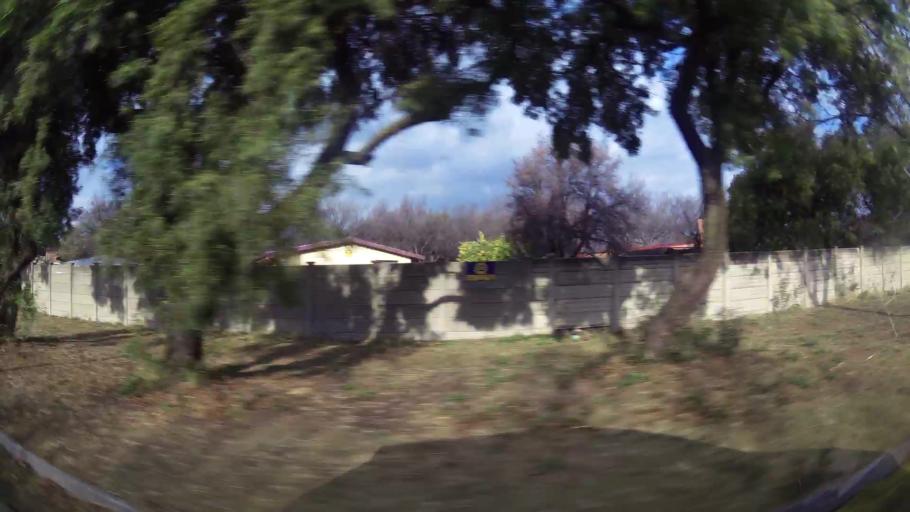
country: ZA
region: Orange Free State
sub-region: Fezile Dabi District Municipality
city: Sasolburg
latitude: -26.8053
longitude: 27.8124
